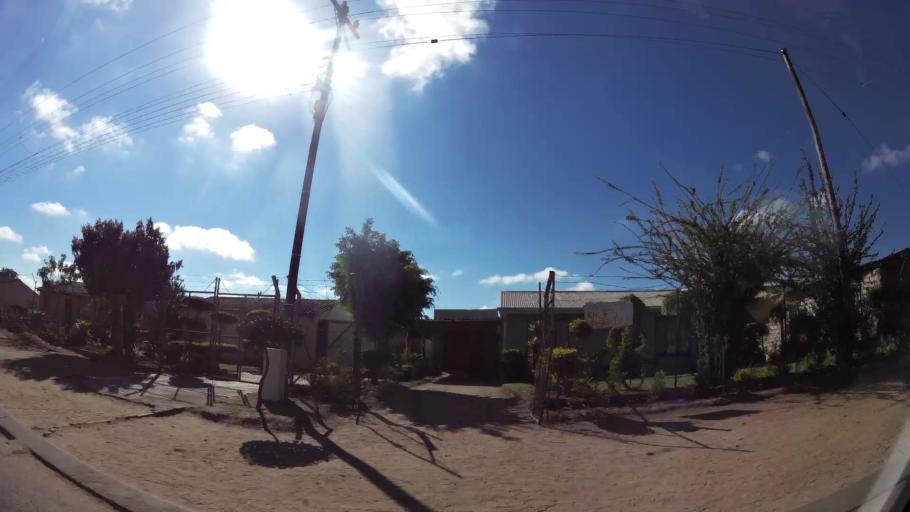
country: ZA
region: Limpopo
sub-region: Capricorn District Municipality
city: Polokwane
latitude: -23.8629
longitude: 29.3851
